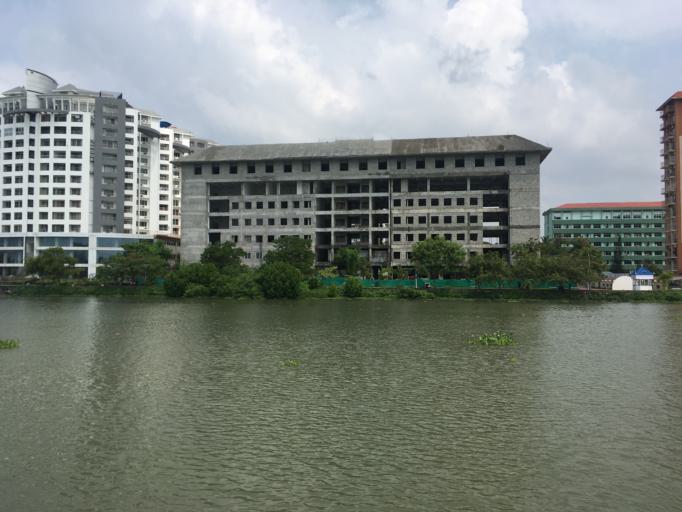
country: IN
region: Kerala
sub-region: Ernakulam
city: Cochin
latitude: 9.9880
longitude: 76.2698
